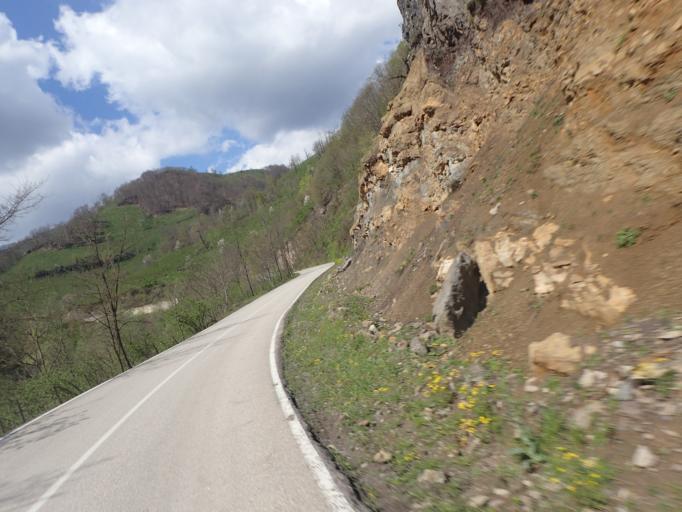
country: TR
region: Ordu
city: Korgan
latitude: 40.7630
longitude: 37.3253
